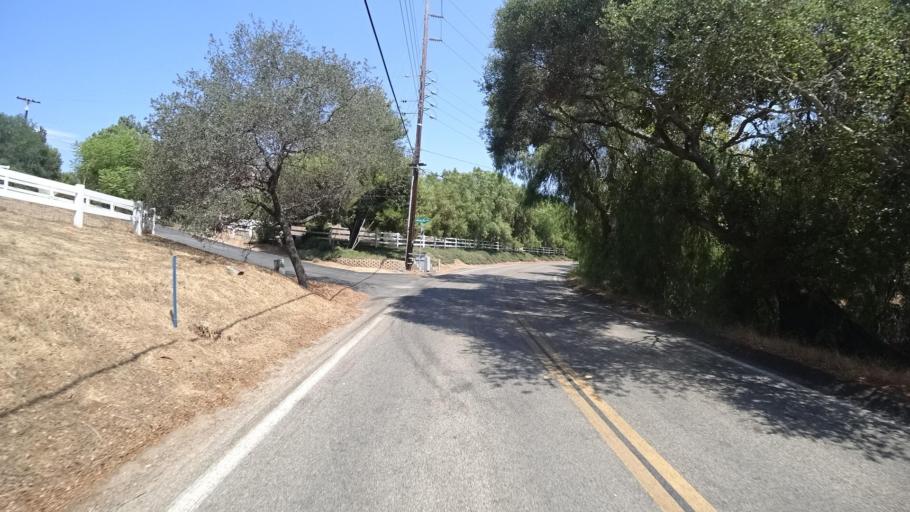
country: US
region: California
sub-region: San Diego County
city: Fallbrook
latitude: 33.3367
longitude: -117.2314
